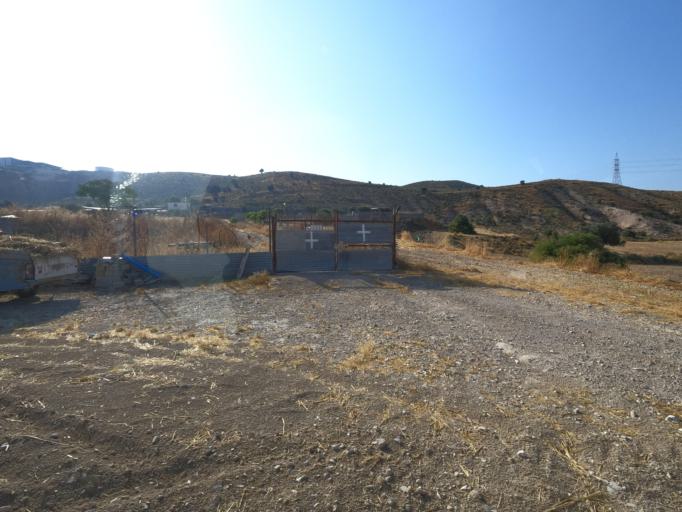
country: CY
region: Lefkosia
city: Lympia
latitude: 34.9857
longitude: 33.4576
